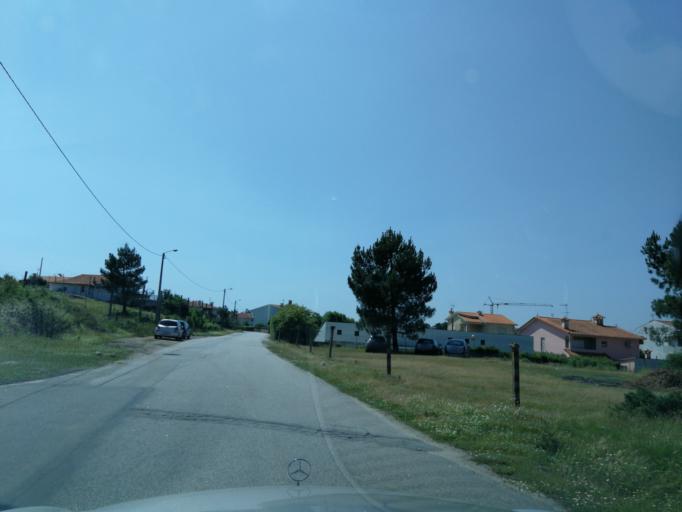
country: PT
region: Braga
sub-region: Braga
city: Adaufe
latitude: 41.5569
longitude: -8.3493
